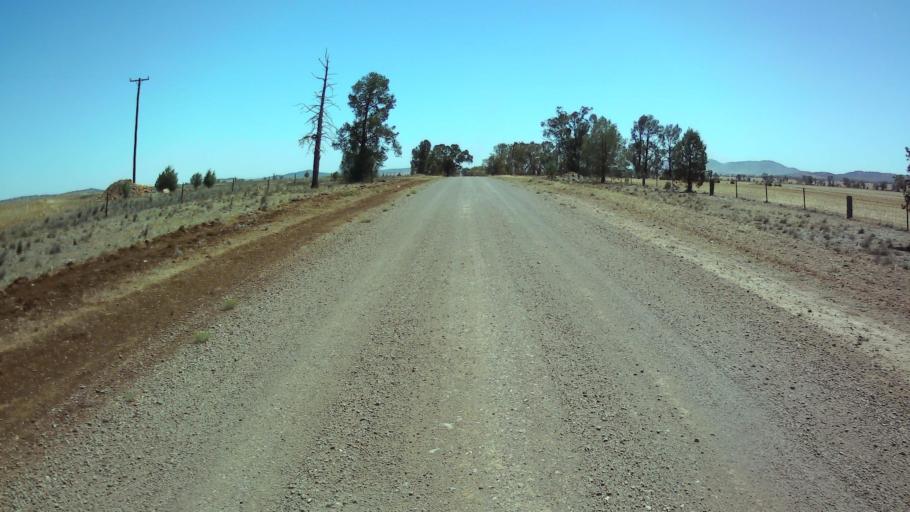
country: AU
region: New South Wales
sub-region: Forbes
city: Forbes
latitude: -33.6926
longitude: 147.7082
